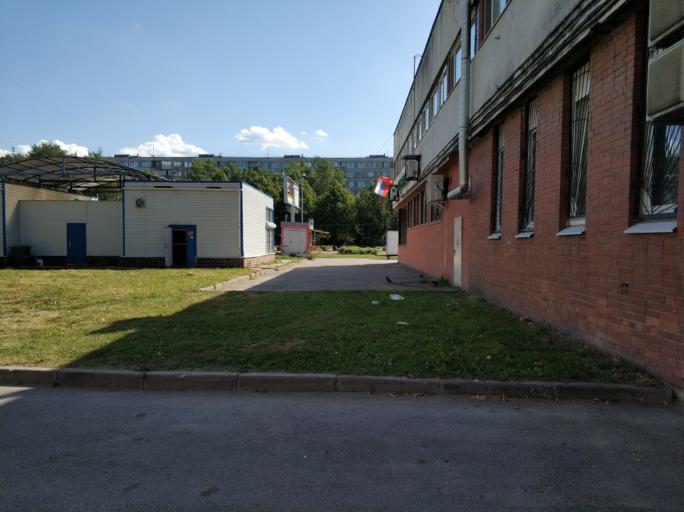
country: RU
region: Leningrad
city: Akademicheskoe
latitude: 60.0165
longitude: 30.3993
